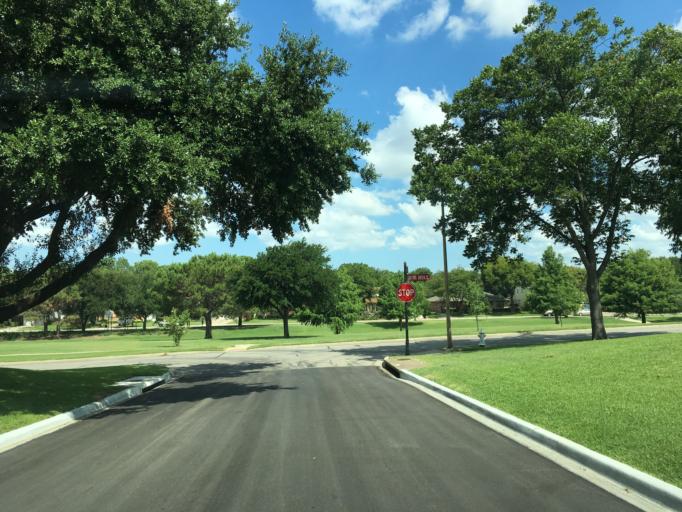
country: US
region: Texas
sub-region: Dallas County
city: Farmers Branch
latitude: 32.9294
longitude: -96.8786
